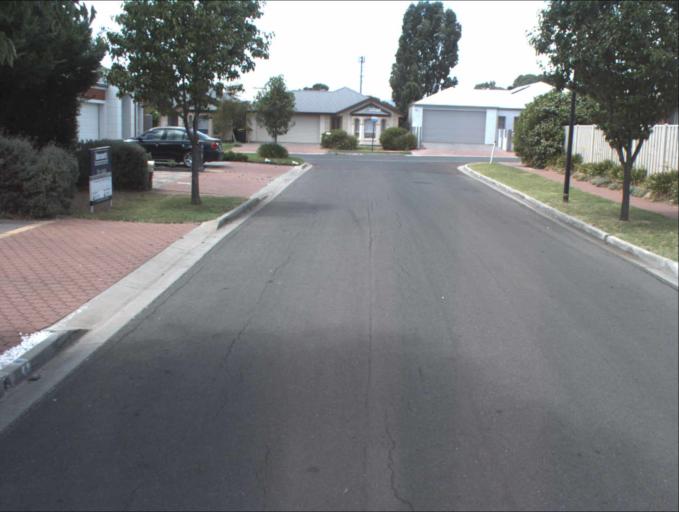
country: AU
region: South Australia
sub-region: Salisbury
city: Ingle Farm
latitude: -34.8485
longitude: 138.6300
